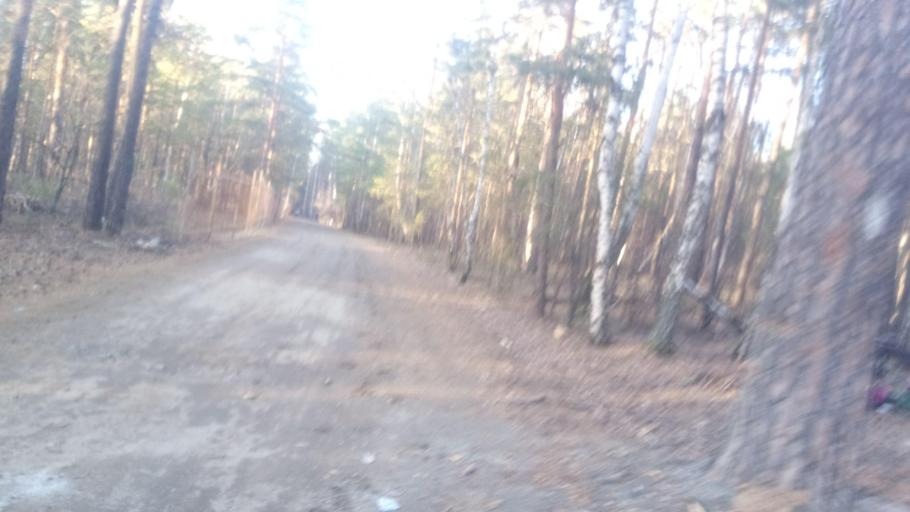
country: RU
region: Chelyabinsk
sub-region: Gorod Chelyabinsk
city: Chelyabinsk
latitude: 55.1276
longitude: 61.3481
